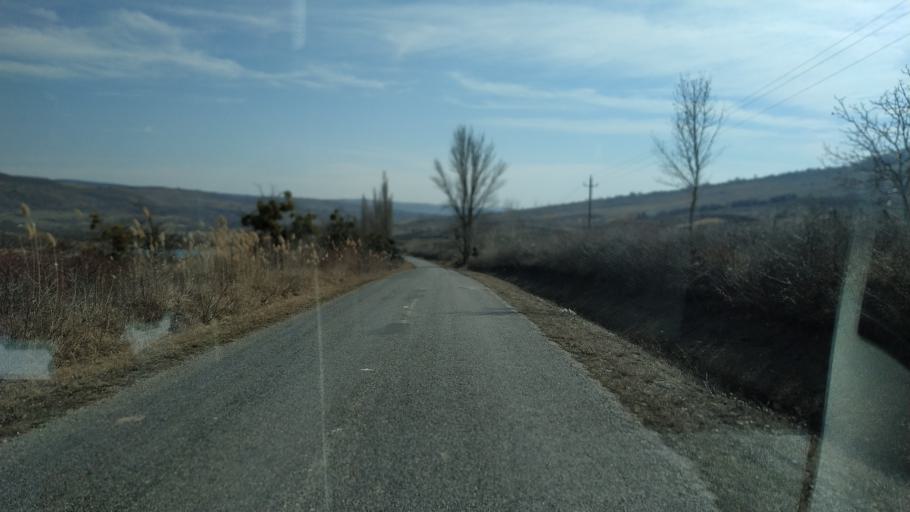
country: MD
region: Nisporeni
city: Nisporeni
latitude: 47.1735
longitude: 28.0882
